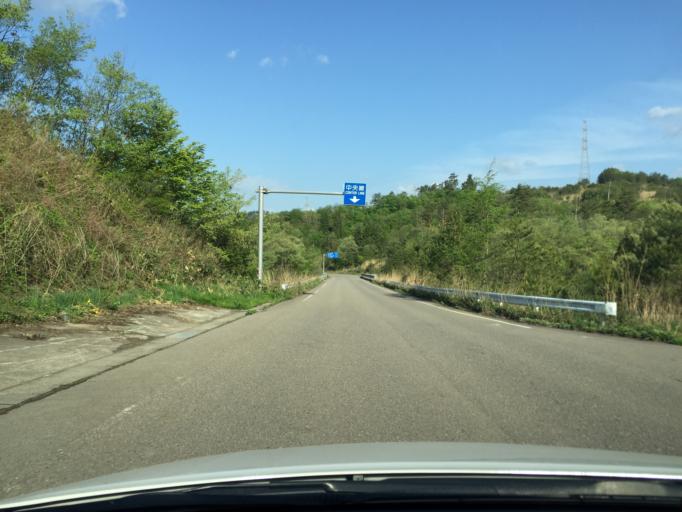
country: JP
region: Fukushima
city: Kitakata
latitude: 37.6703
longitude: 139.8180
